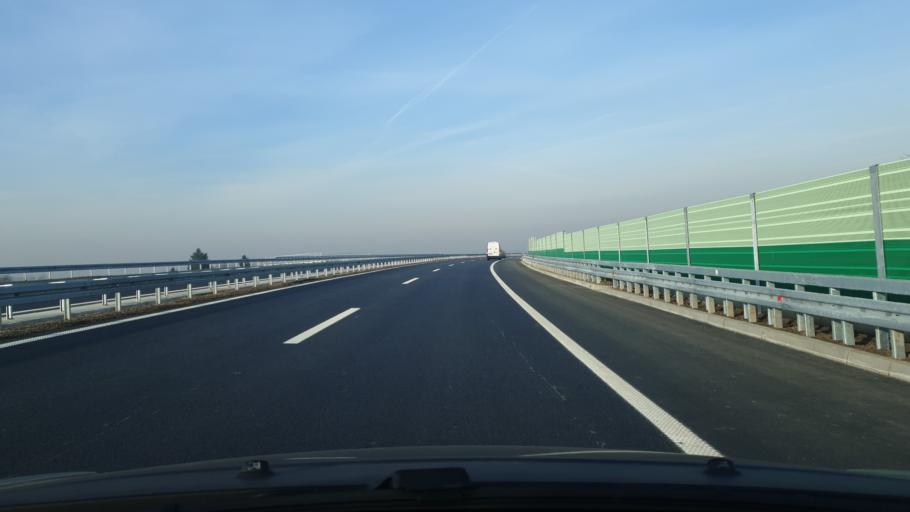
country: RS
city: Boljevci
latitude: 44.7314
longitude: 20.2464
